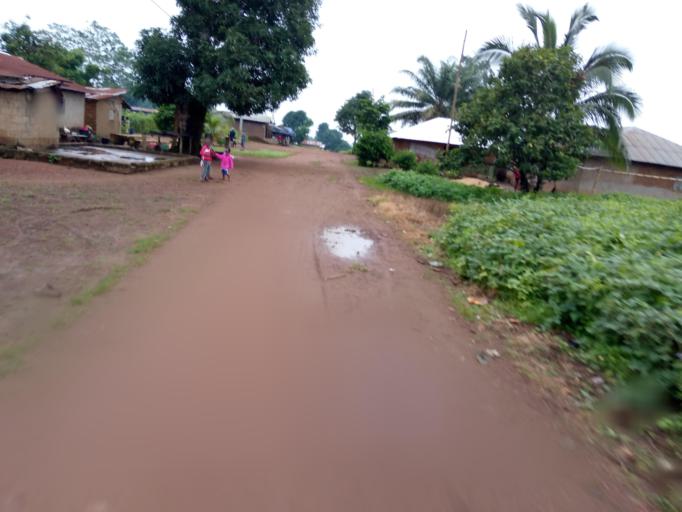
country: SL
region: Eastern Province
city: Buedu
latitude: 8.4665
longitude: -10.3432
